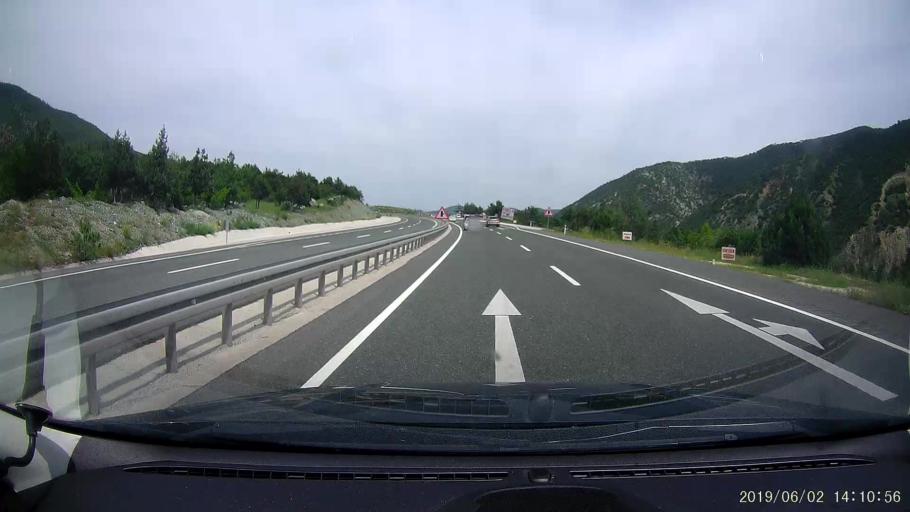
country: TR
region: Cankiri
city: Yaprakli
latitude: 40.9053
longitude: 33.7747
